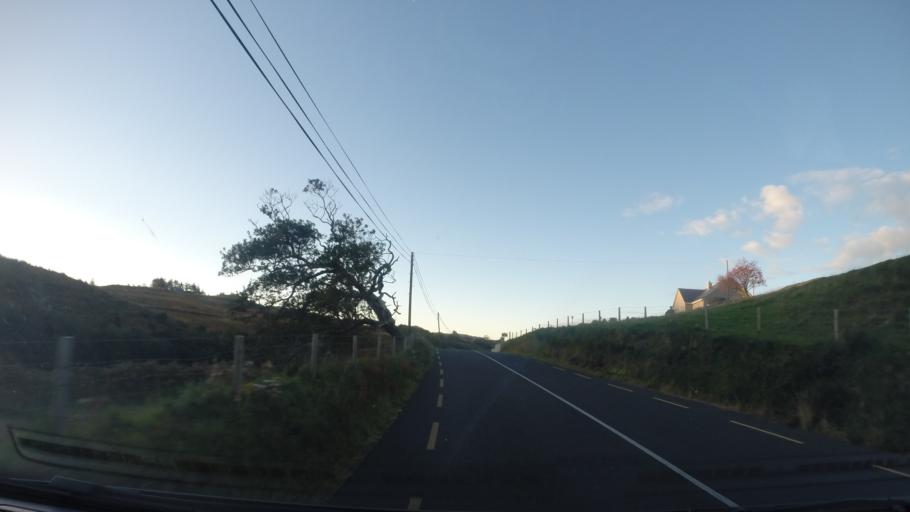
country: IE
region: Ulster
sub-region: County Donegal
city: Killybegs
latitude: 54.6551
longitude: -8.6372
